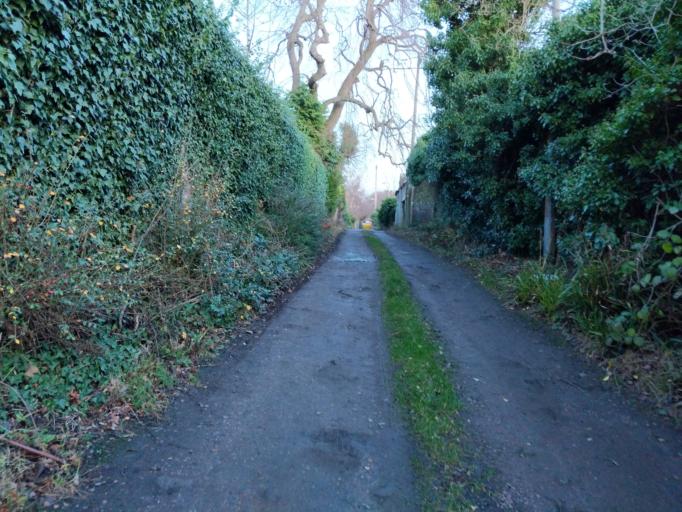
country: GB
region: Scotland
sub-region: Edinburgh
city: Edinburgh
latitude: 55.9305
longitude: -3.2147
